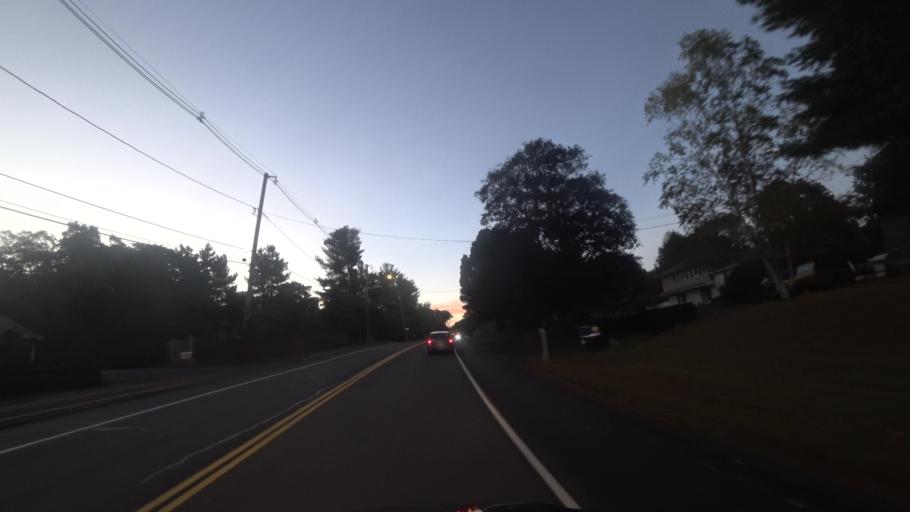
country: US
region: Massachusetts
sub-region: Middlesex County
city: Wakefield
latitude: 42.4919
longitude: -71.0502
